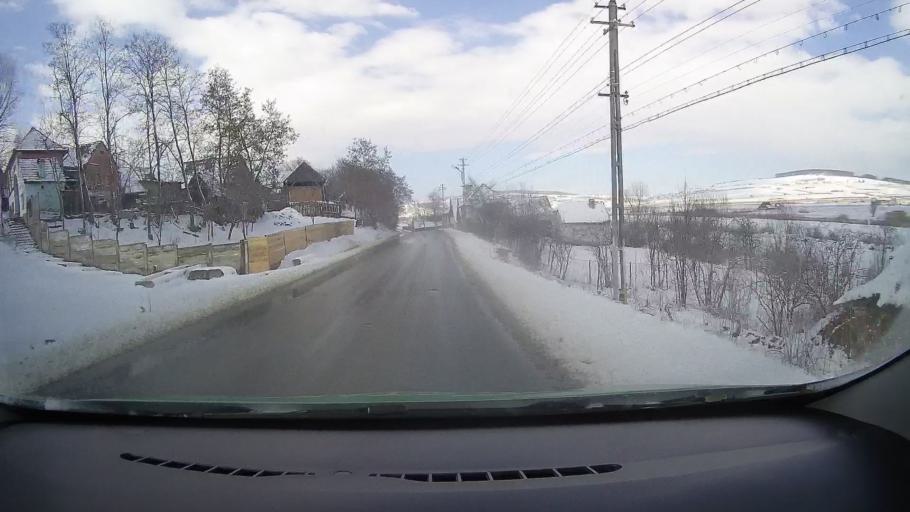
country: RO
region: Sibiu
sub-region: Comuna Altina
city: Altina
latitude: 45.9336
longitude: 24.4640
